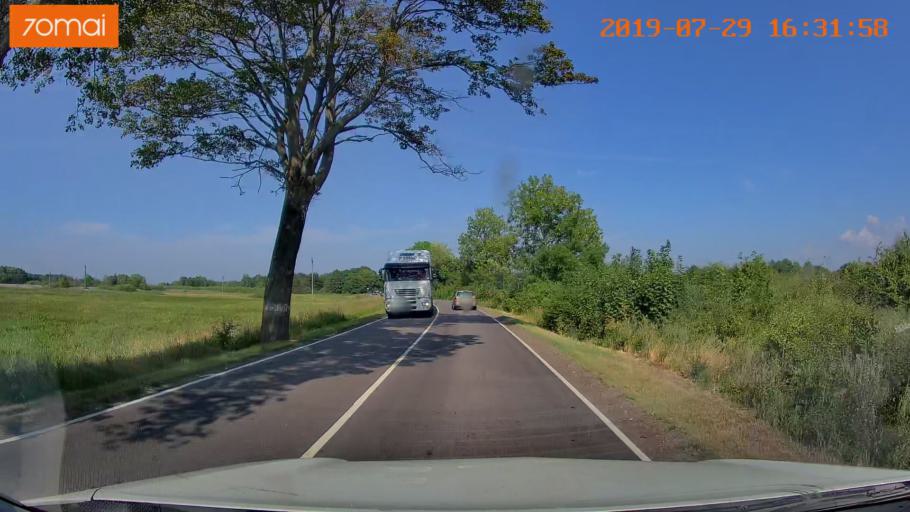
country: RU
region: Kaliningrad
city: Primorsk
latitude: 54.7327
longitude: 20.0199
